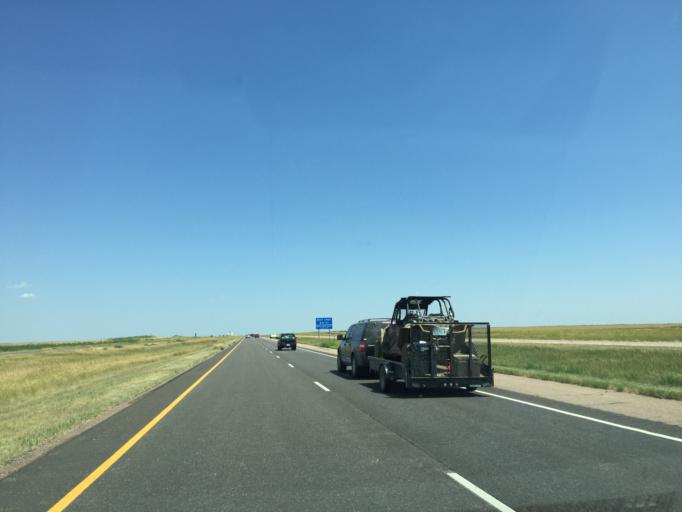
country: US
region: Colorado
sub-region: Lincoln County
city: Hugo
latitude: 39.2815
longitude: -103.3289
